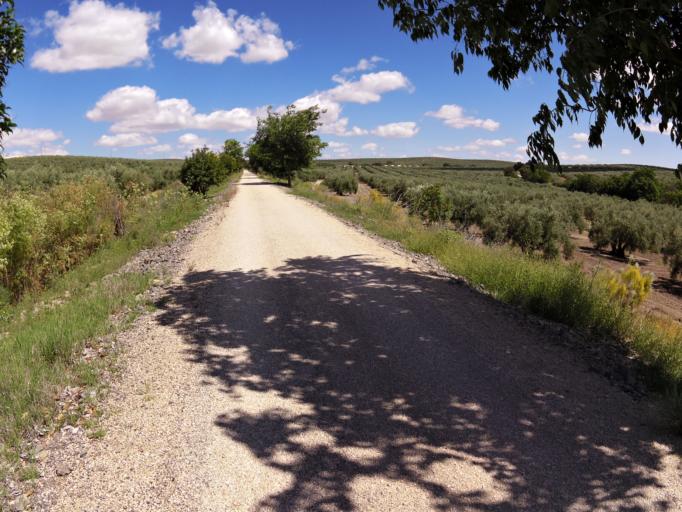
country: ES
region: Andalusia
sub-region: Provincia de Jaen
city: Alcaudete
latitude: 37.6548
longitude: -4.0619
